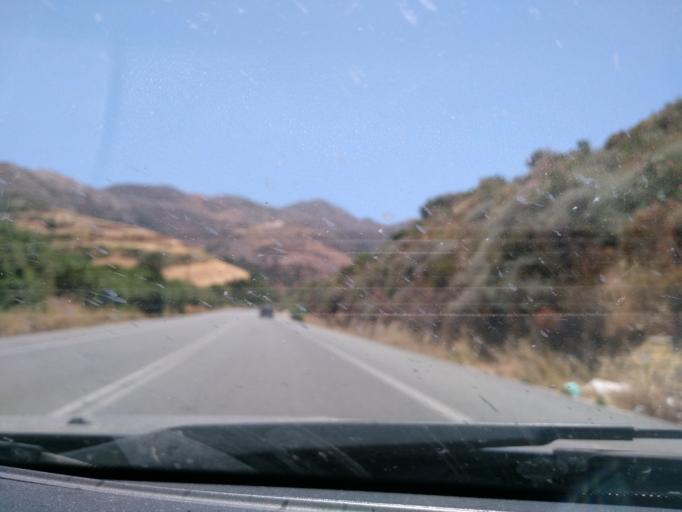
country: GR
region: Crete
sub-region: Nomos Rethymnis
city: Anogeia
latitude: 35.3907
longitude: 24.9205
